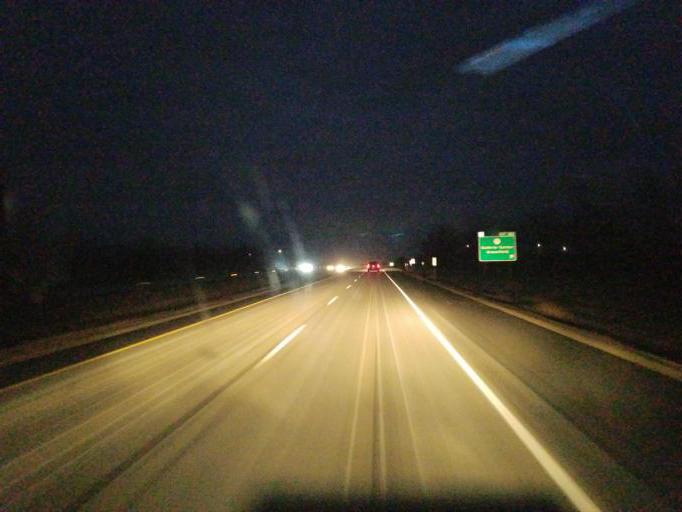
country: US
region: Iowa
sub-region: Guthrie County
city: Stuart
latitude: 41.4958
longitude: -94.4585
